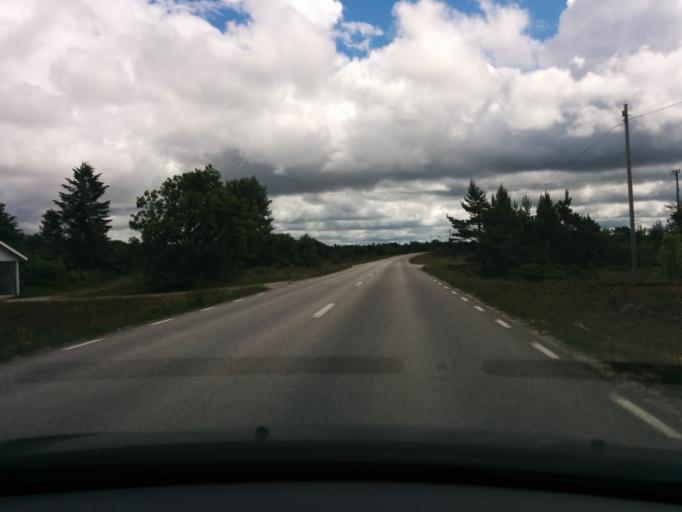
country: SE
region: Gotland
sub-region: Gotland
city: Visby
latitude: 57.6380
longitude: 18.3690
